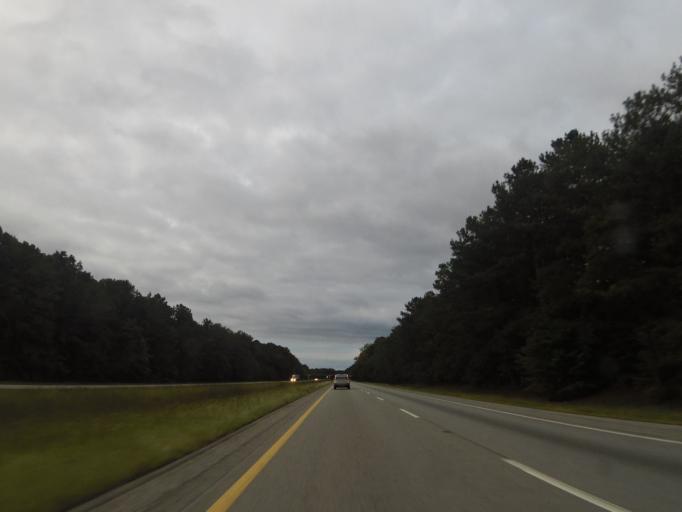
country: US
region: Alabama
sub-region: Saint Clair County
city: Springville
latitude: 33.8059
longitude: -86.3634
